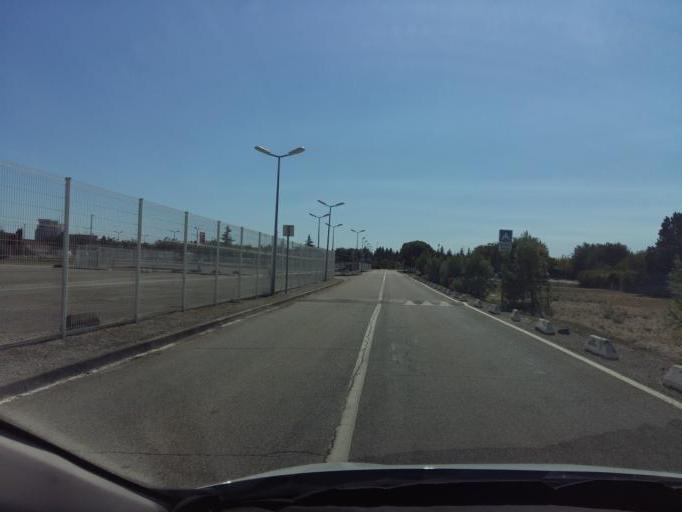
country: FR
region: Provence-Alpes-Cote d'Azur
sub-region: Departement des Bouches-du-Rhone
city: Noves
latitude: 43.9066
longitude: 4.8966
